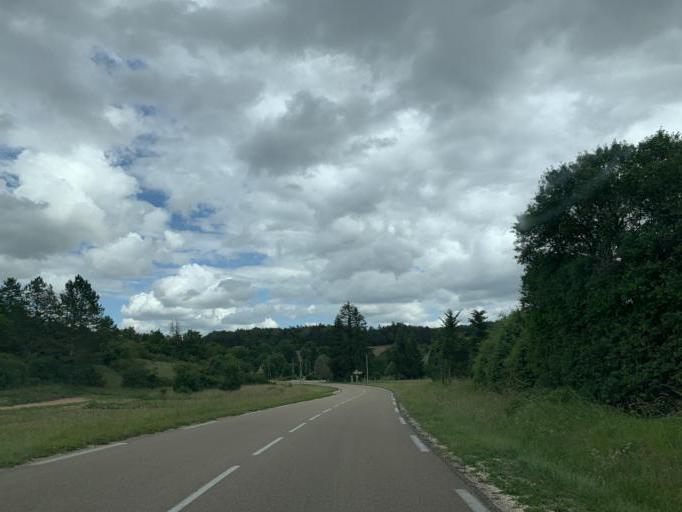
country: FR
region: Bourgogne
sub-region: Departement de l'Yonne
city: Chablis
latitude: 47.7340
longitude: 3.7981
